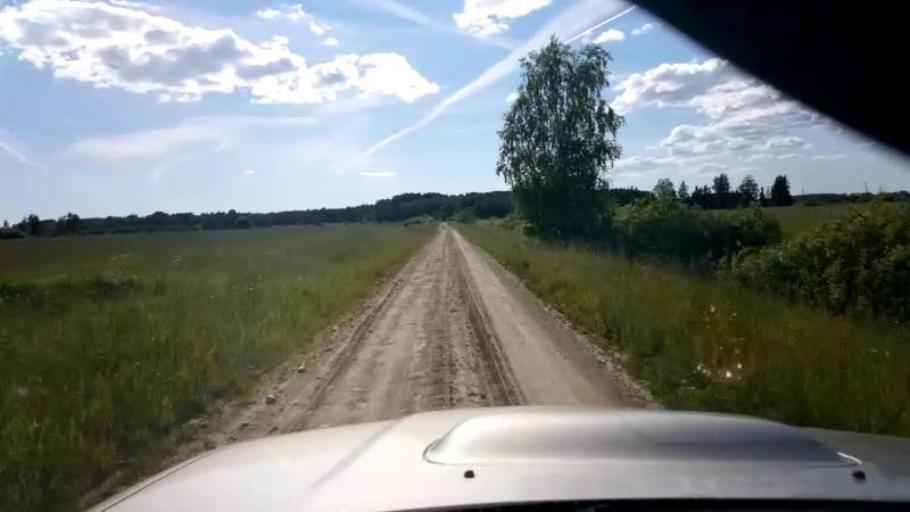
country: EE
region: Paernumaa
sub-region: Sauga vald
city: Sauga
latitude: 58.4910
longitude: 24.5556
